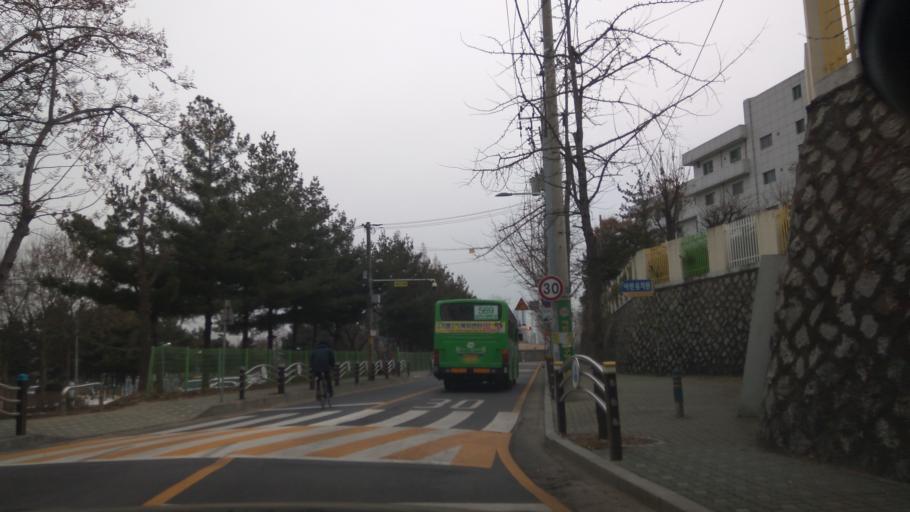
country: KR
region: Incheon
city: Incheon
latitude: 37.4945
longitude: 126.7086
